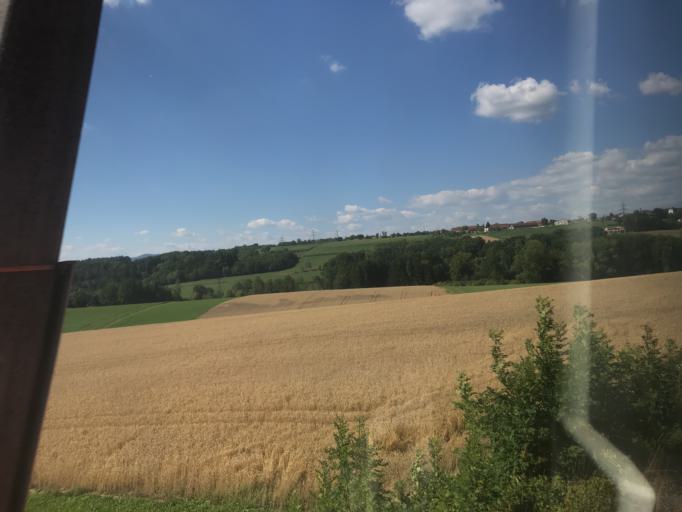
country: AT
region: Upper Austria
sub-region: Politischer Bezirk Urfahr-Umgebung
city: Engerwitzdorf
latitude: 48.3234
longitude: 14.4946
